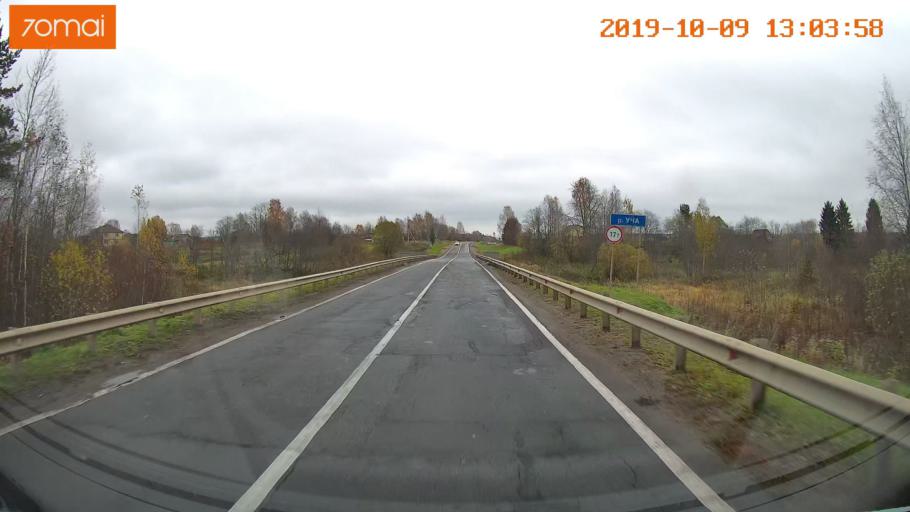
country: RU
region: Jaroslavl
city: Lyubim
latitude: 58.3587
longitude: 40.5425
